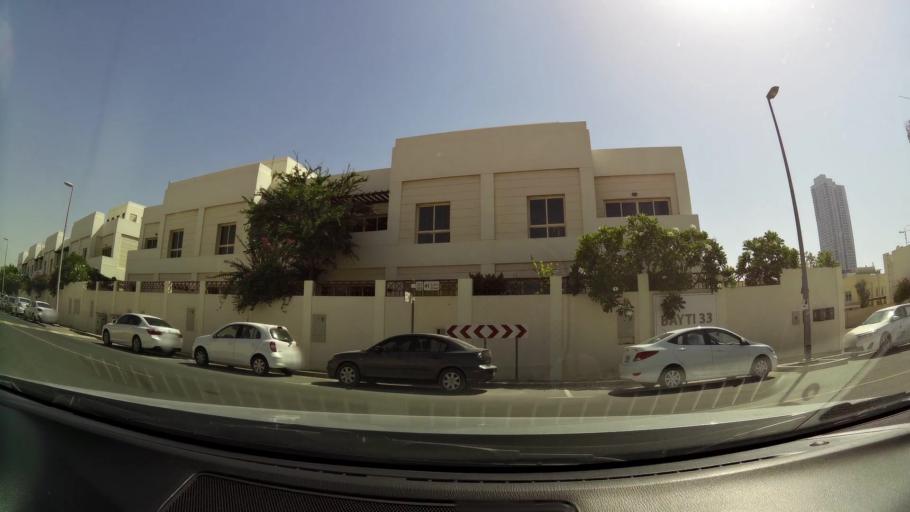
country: AE
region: Dubai
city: Dubai
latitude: 25.1073
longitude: 55.1849
